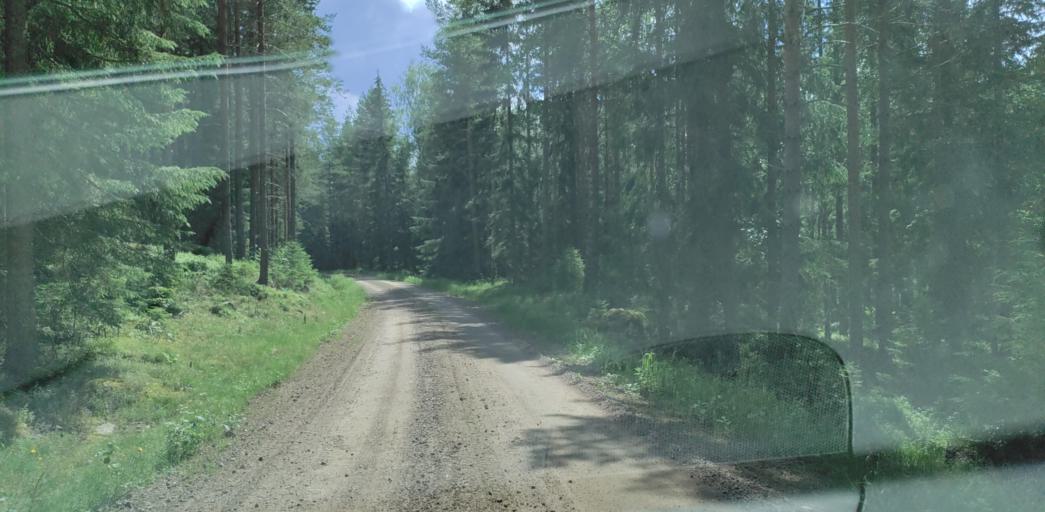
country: SE
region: Vaermland
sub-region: Hagfors Kommun
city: Ekshaerad
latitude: 60.0841
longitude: 13.3449
